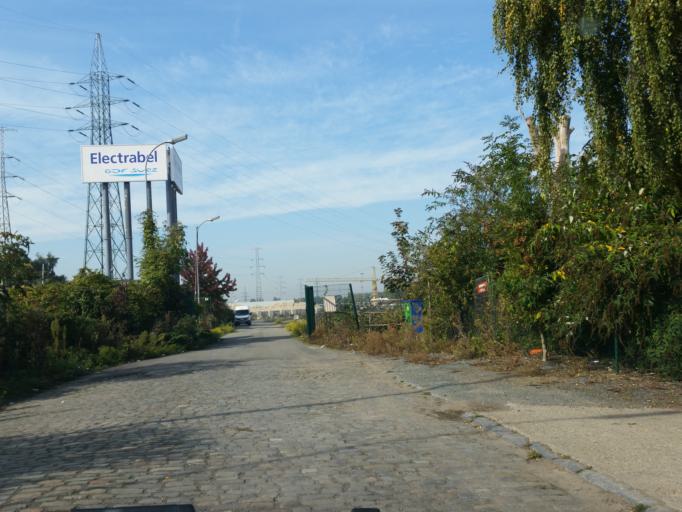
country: BE
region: Flanders
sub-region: Provincie Vlaams-Brabant
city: Drogenbos
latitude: 50.8049
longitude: 4.3013
